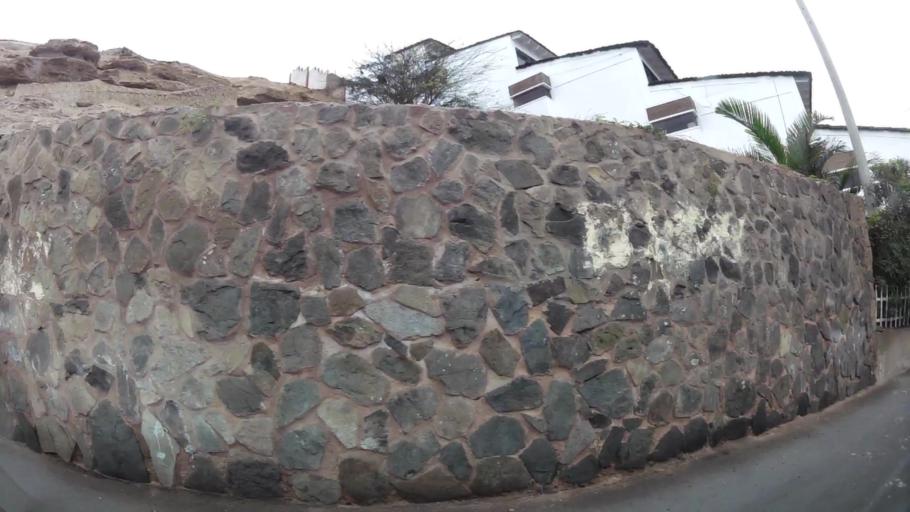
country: PE
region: Lima
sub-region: Lima
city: Punta Hermosa
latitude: -12.3391
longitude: -76.8183
